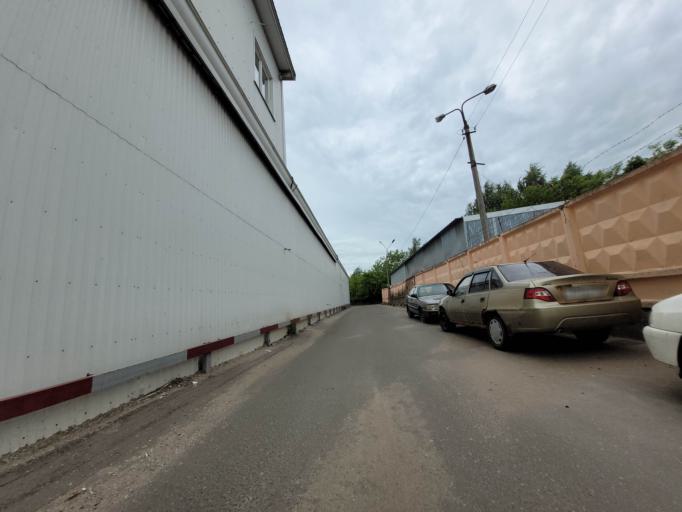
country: RU
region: Moskovskaya
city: Yubileyny
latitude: 55.9428
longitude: 37.8484
